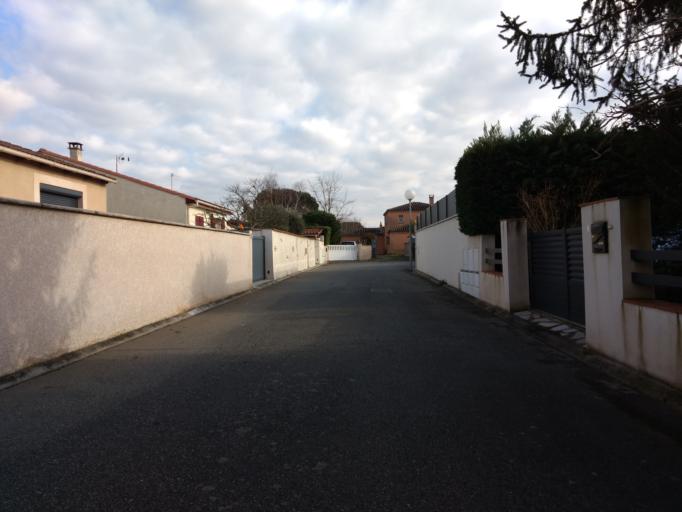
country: FR
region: Midi-Pyrenees
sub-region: Departement de la Haute-Garonne
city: Tournefeuille
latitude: 43.5815
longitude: 1.3554
